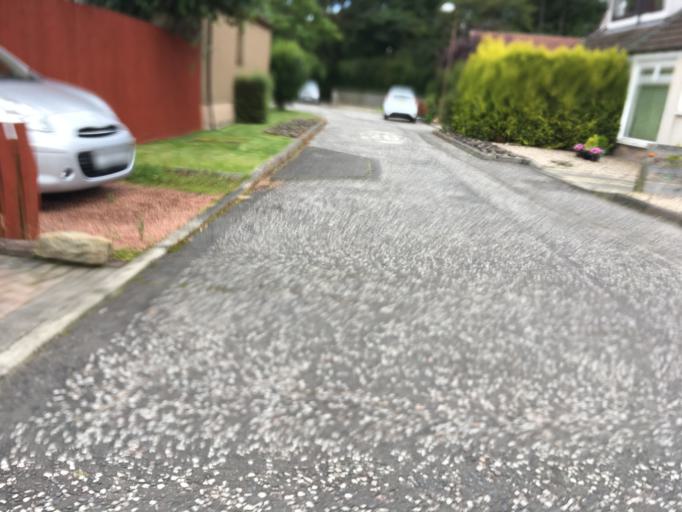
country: GB
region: Scotland
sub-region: West Lothian
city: Mid Calder
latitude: 55.8737
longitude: -3.5033
